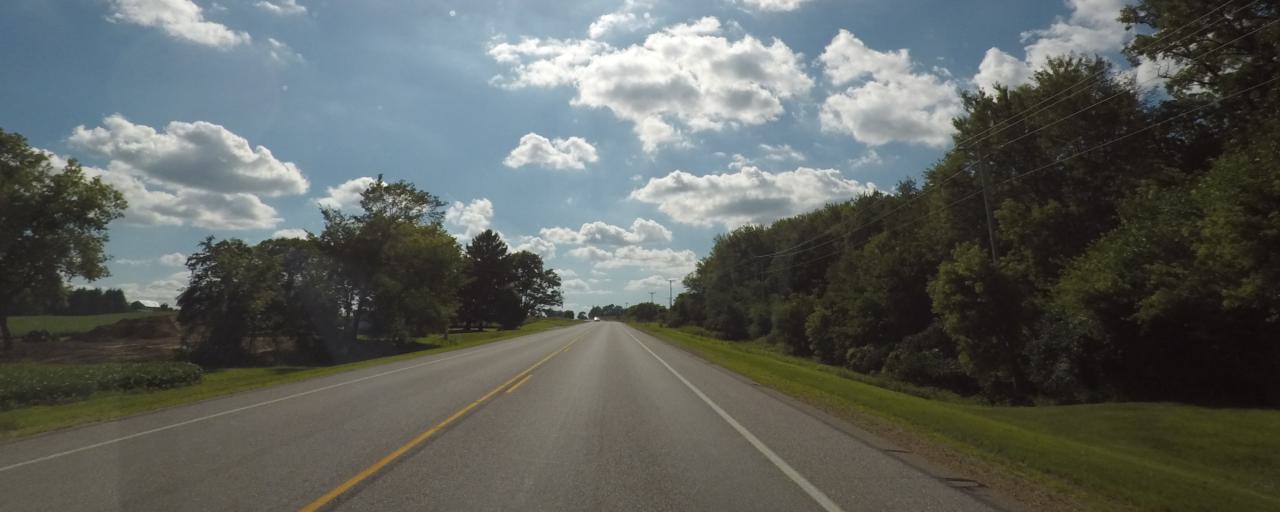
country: US
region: Wisconsin
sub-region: Dane County
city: Stoughton
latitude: 42.9198
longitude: -89.1274
